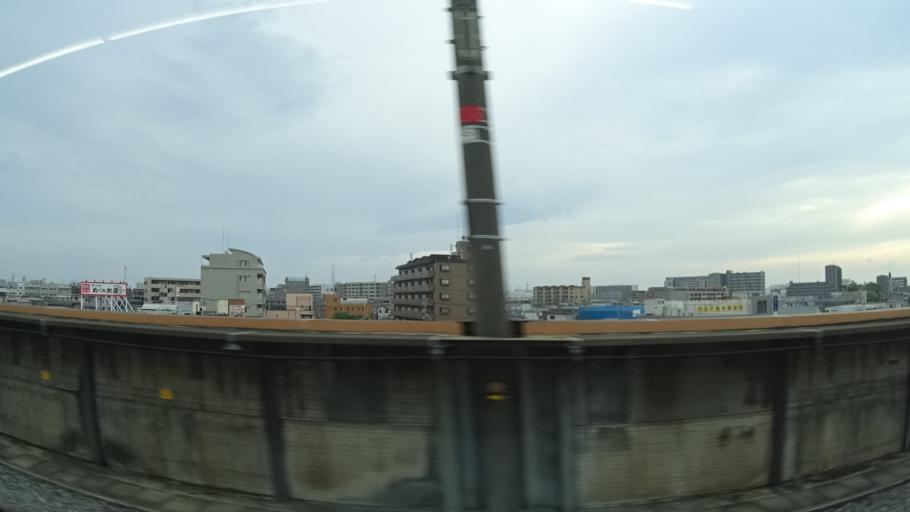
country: JP
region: Saitama
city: Shimotoda
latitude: 35.8080
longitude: 139.6778
